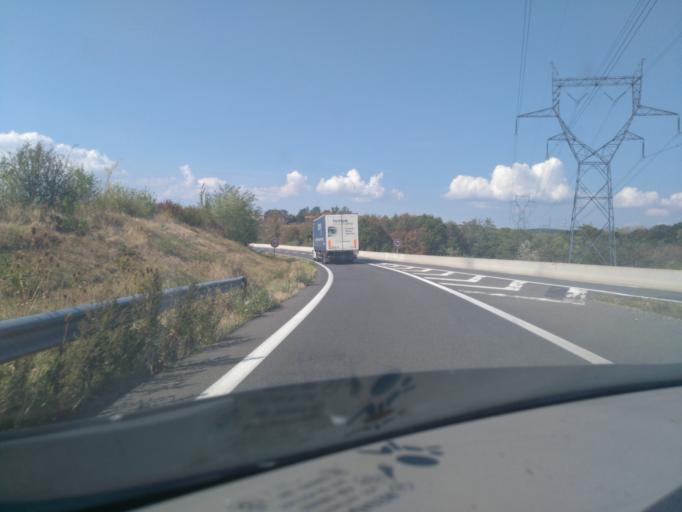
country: FR
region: Rhone-Alpes
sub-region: Departement du Rhone
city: Lozanne
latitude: 45.8550
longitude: 4.6579
